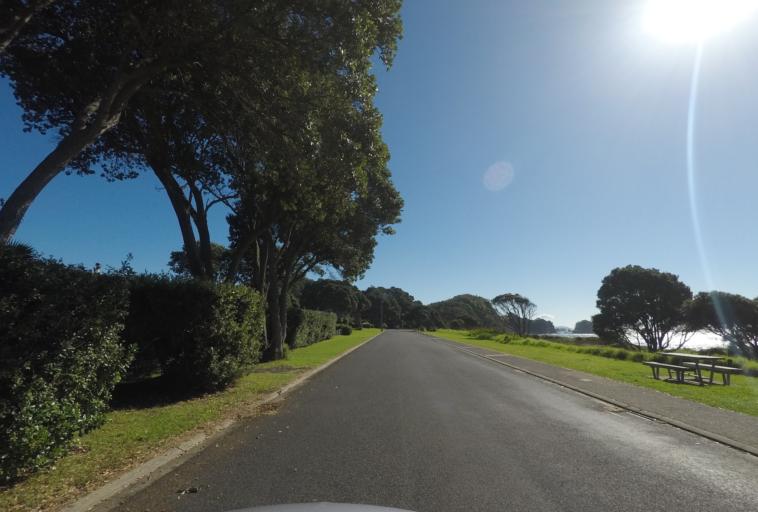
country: NZ
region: Waikato
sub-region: Thames-Coromandel District
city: Whangamata
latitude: -37.2812
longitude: 175.9014
